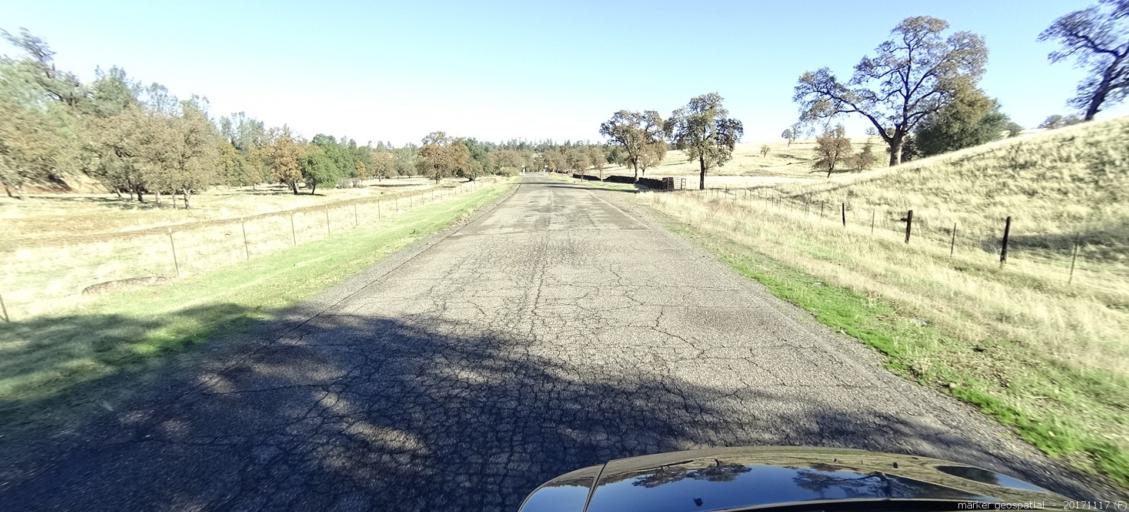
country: US
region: California
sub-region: Shasta County
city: Cottonwood
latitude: 40.4351
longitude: -122.1653
